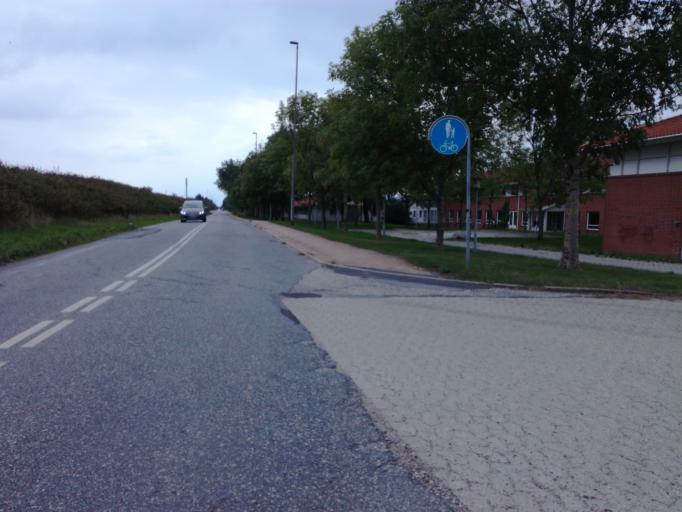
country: DK
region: South Denmark
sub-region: Fredericia Kommune
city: Fredericia
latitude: 55.5958
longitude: 9.7678
